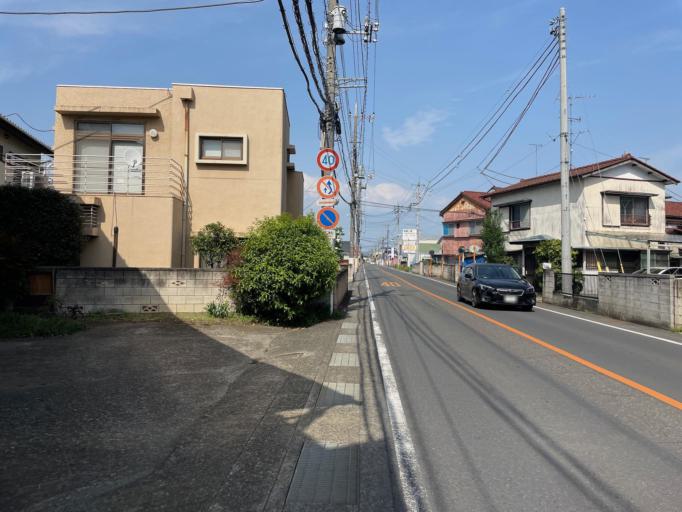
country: JP
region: Gunma
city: Ota
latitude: 36.2948
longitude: 139.3881
